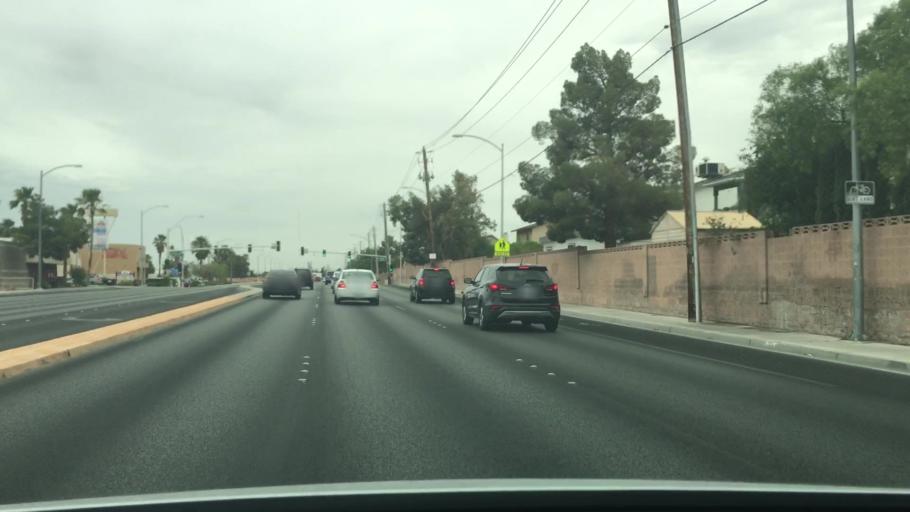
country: US
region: Nevada
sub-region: Clark County
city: Spring Valley
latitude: 36.1679
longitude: -115.2600
